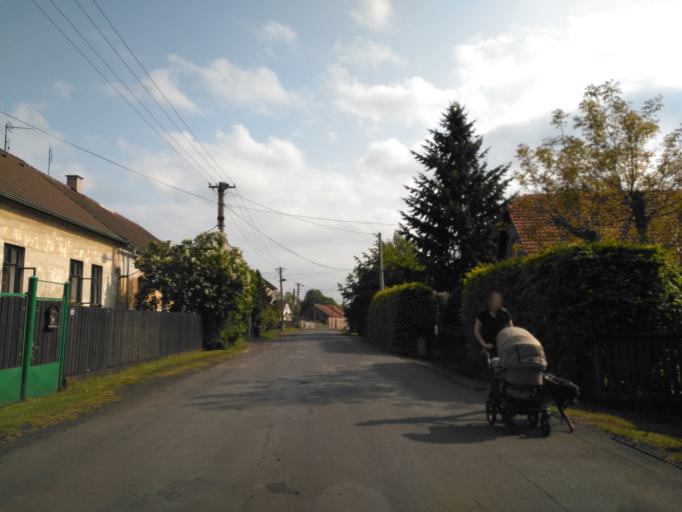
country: CZ
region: Plzensky
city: Zbiroh
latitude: 49.8721
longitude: 13.7964
